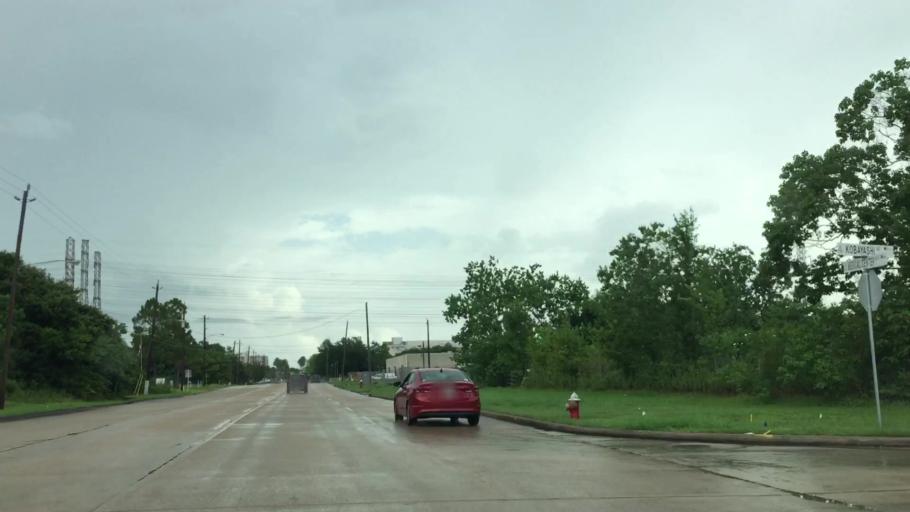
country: US
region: Texas
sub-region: Harris County
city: Webster
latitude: 29.5361
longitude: -95.1333
